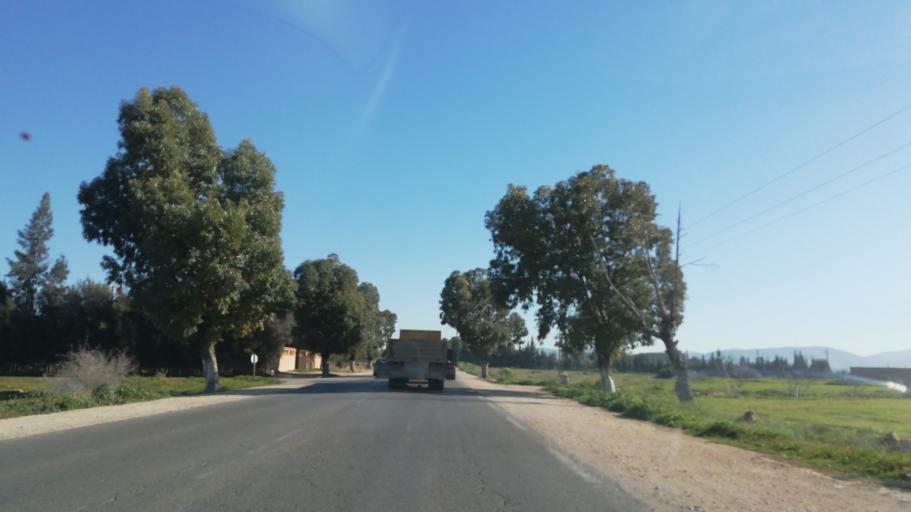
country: DZ
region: Relizane
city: Zemoura
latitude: 35.7451
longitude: 0.6987
